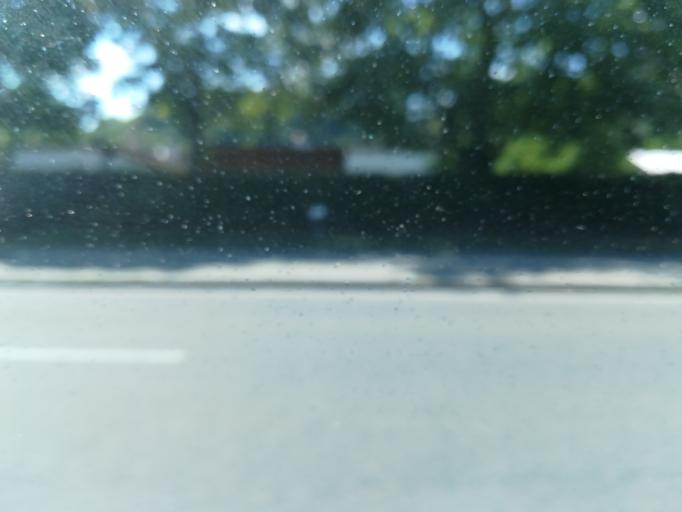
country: DE
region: Baden-Wuerttemberg
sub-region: Freiburg Region
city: Singen
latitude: 47.7555
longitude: 8.8205
